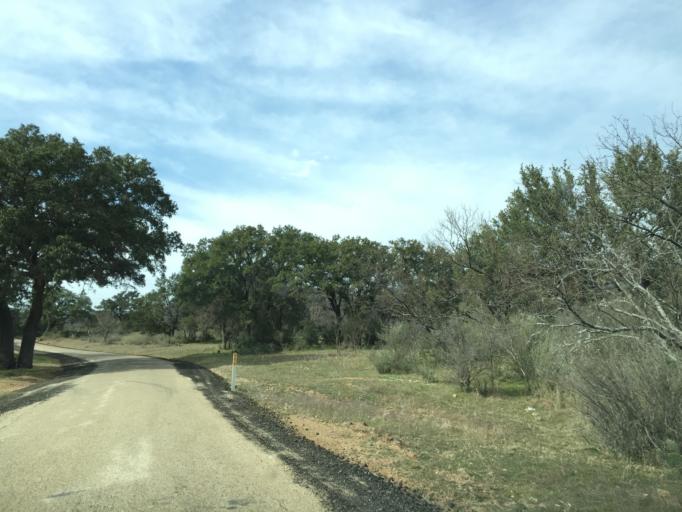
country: US
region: Texas
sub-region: Gillespie County
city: Fredericksburg
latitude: 30.4478
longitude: -98.6583
